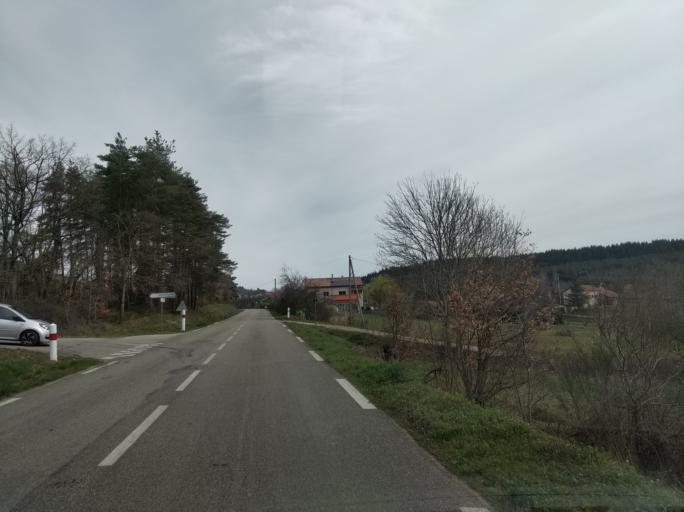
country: FR
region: Rhone-Alpes
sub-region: Departement de l'Ardeche
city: Satillieu
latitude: 45.1681
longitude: 4.6363
